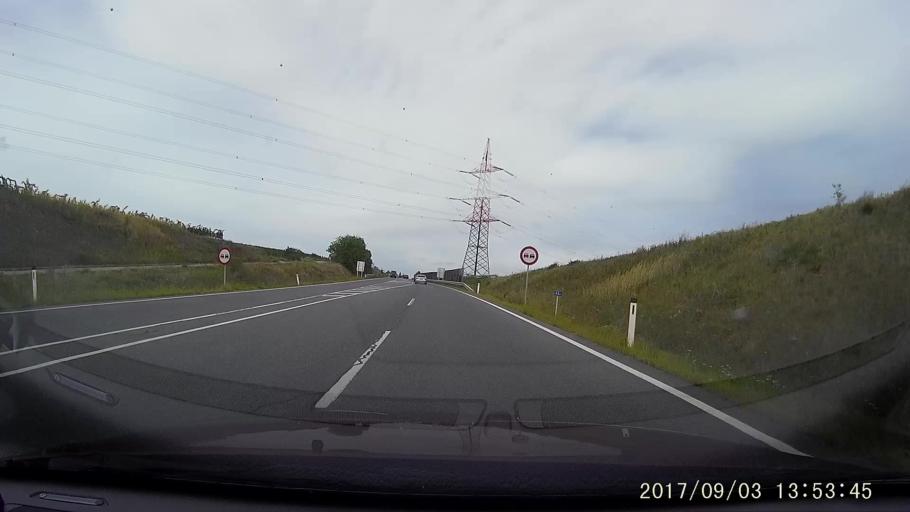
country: AT
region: Lower Austria
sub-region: Politischer Bezirk Hollabrunn
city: Haugsdorf
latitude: 48.7356
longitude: 16.0585
